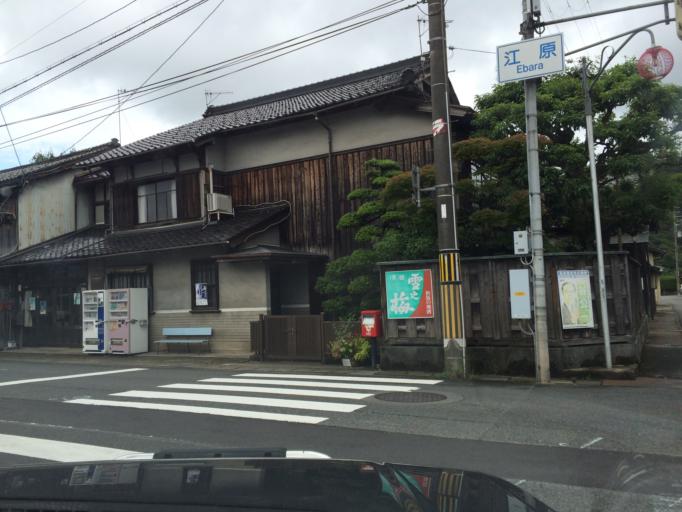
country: JP
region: Hyogo
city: Toyooka
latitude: 35.4670
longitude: 134.7756
